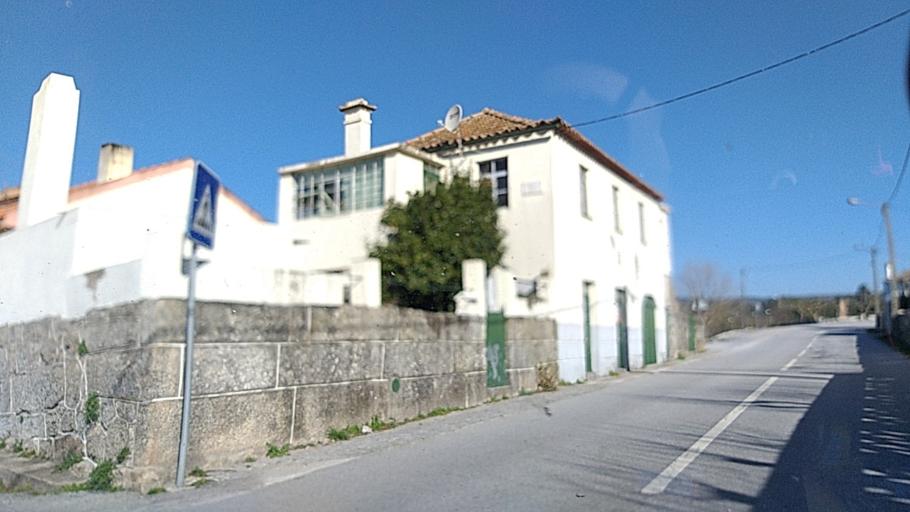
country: PT
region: Guarda
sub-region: Fornos de Algodres
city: Fornos de Algodres
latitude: 40.6306
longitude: -7.4987
